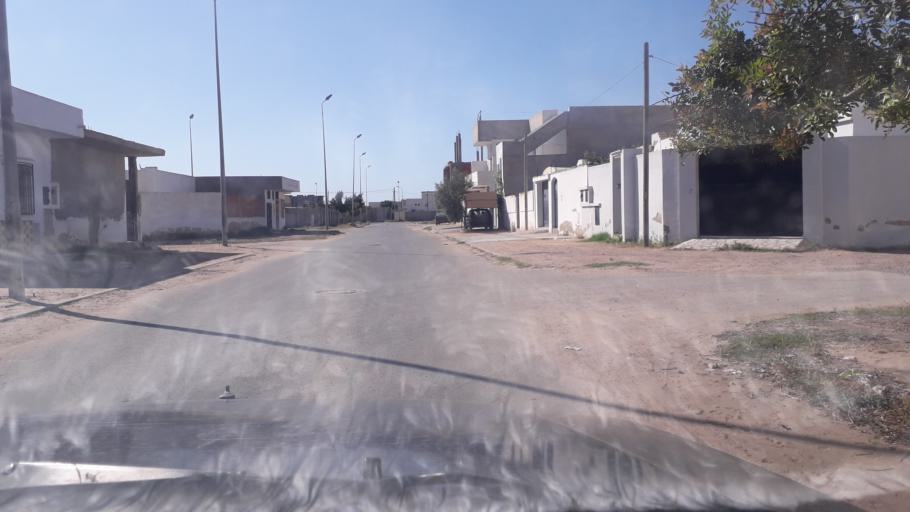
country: TN
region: Safaqis
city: Al Qarmadah
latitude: 34.8253
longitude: 10.7500
